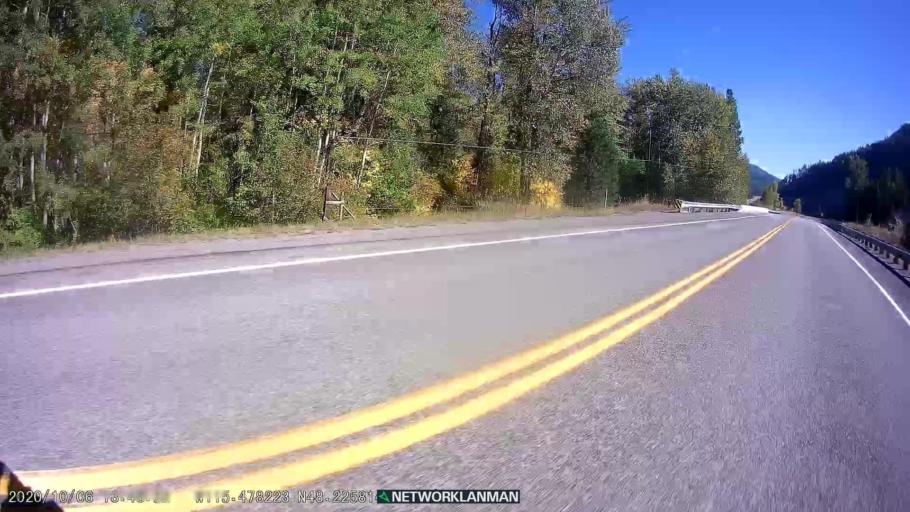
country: US
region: Montana
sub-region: Lincoln County
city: Libby
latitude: 48.2255
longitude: -115.4779
